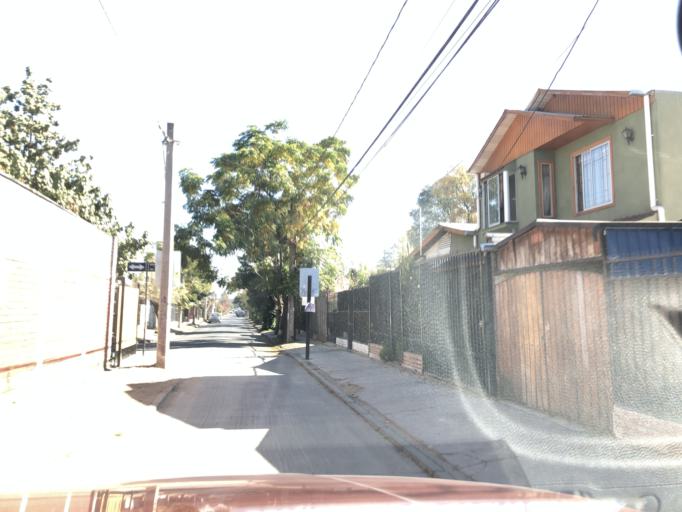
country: CL
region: Santiago Metropolitan
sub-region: Provincia de Cordillera
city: Puente Alto
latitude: -33.5707
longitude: -70.5792
